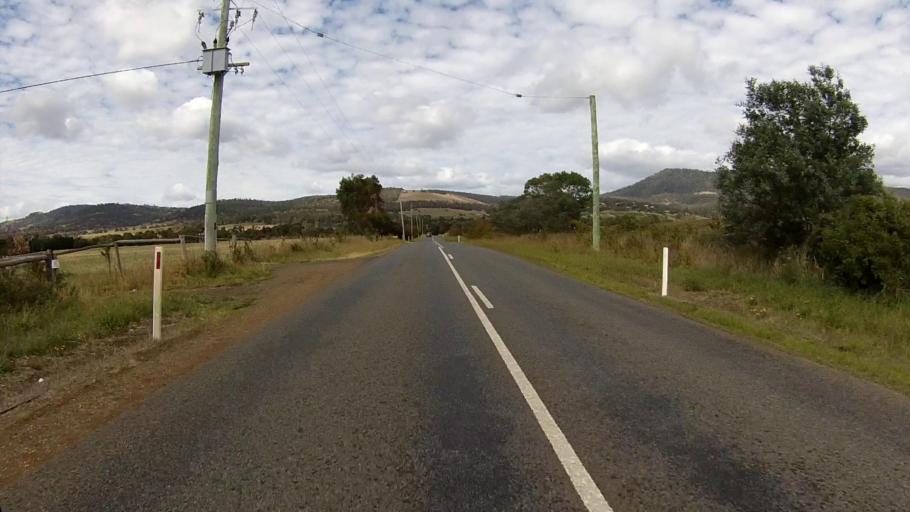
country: AU
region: Tasmania
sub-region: Clarence
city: Cambridge
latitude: -42.7554
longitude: 147.4064
